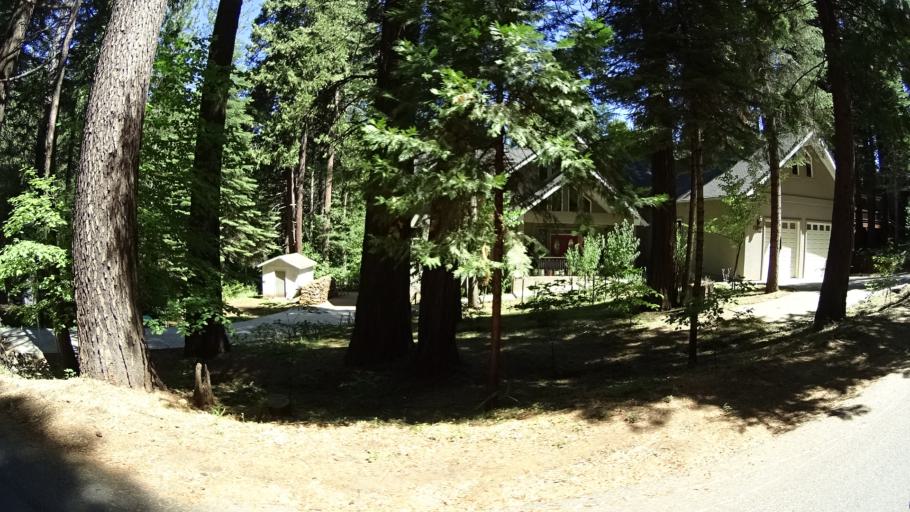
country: US
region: California
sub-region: Calaveras County
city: Arnold
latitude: 38.2342
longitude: -120.3427
